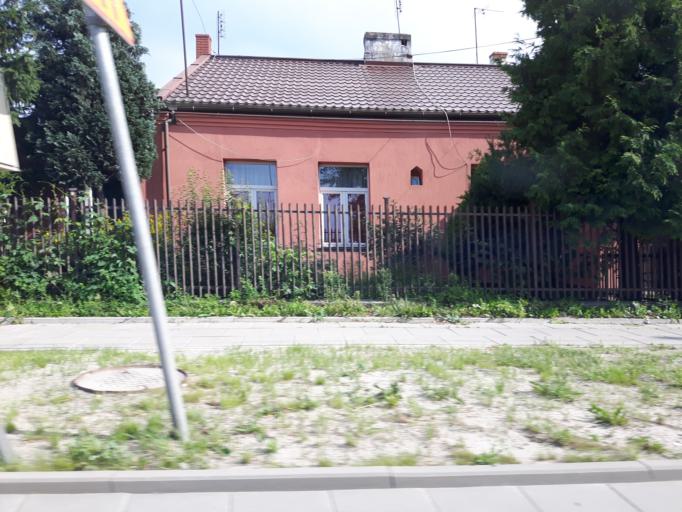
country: PL
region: Masovian Voivodeship
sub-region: Powiat wolominski
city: Zabki
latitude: 52.2730
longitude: 21.0857
